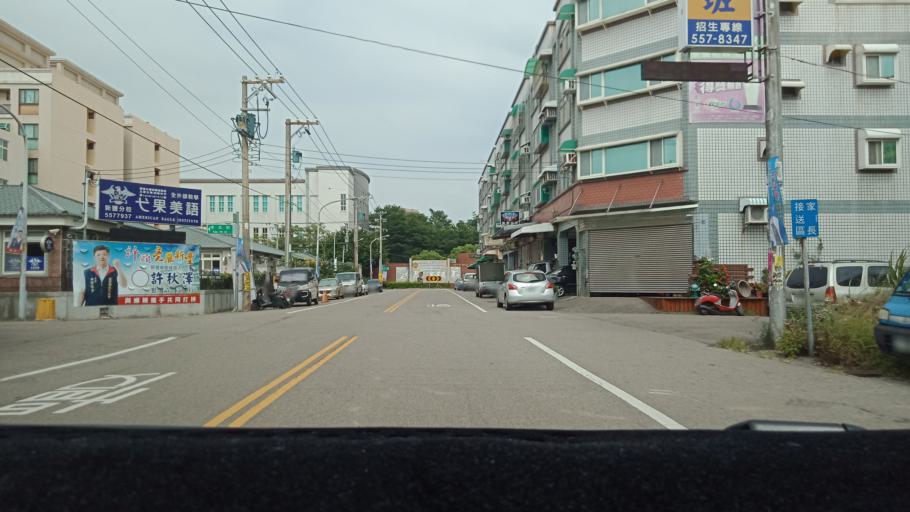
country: TW
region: Taiwan
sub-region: Hsinchu
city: Zhubei
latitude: 24.8784
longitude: 120.9988
